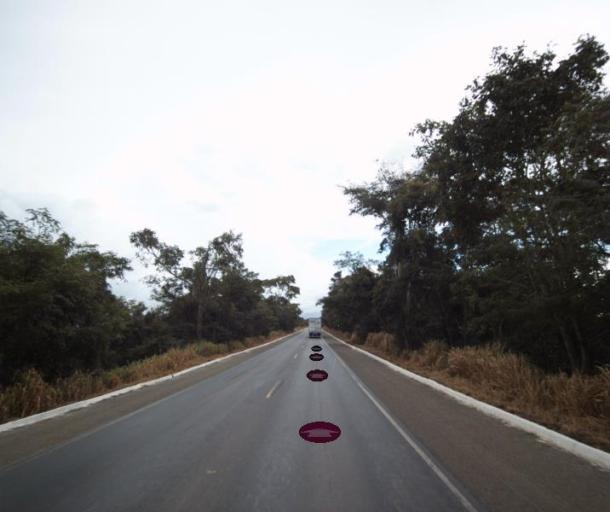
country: BR
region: Goias
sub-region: Itapaci
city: Itapaci
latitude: -14.9137
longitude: -49.3560
